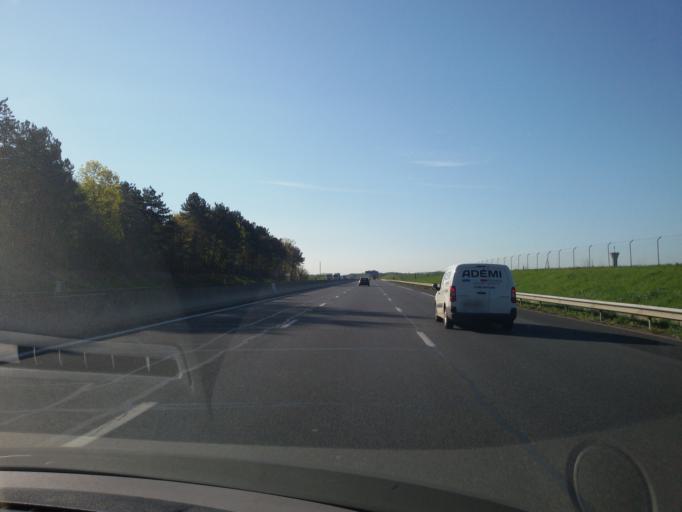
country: FR
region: Ile-de-France
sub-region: Departement de Seine-et-Marne
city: Bagneaux-sur-Loing
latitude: 48.2326
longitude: 2.7568
